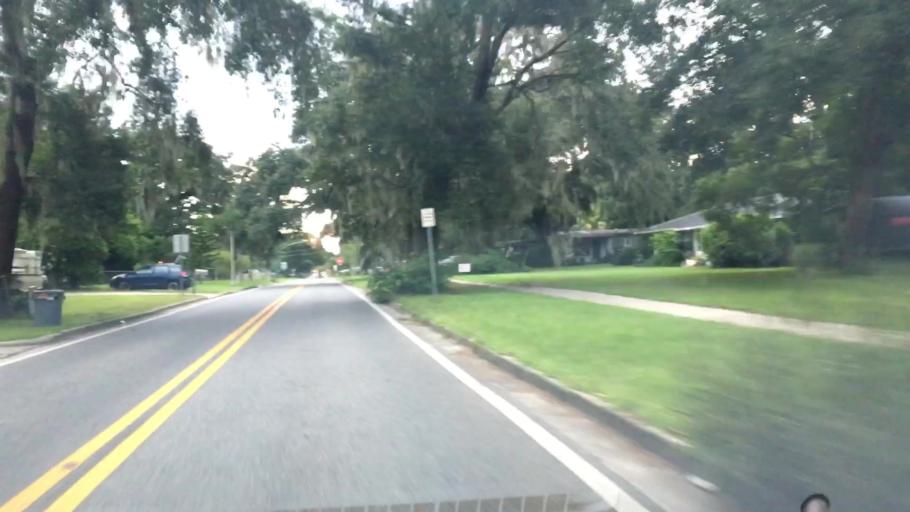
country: US
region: Florida
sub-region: Seminole County
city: Sanford
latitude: 28.7940
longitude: -81.2577
